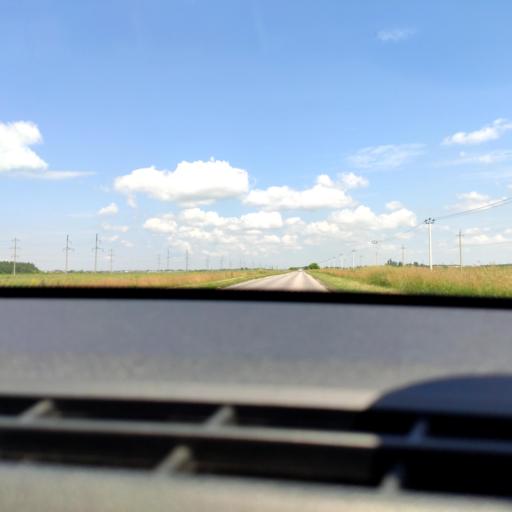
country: RU
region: Samara
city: Podstepki
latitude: 53.5466
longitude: 49.0888
